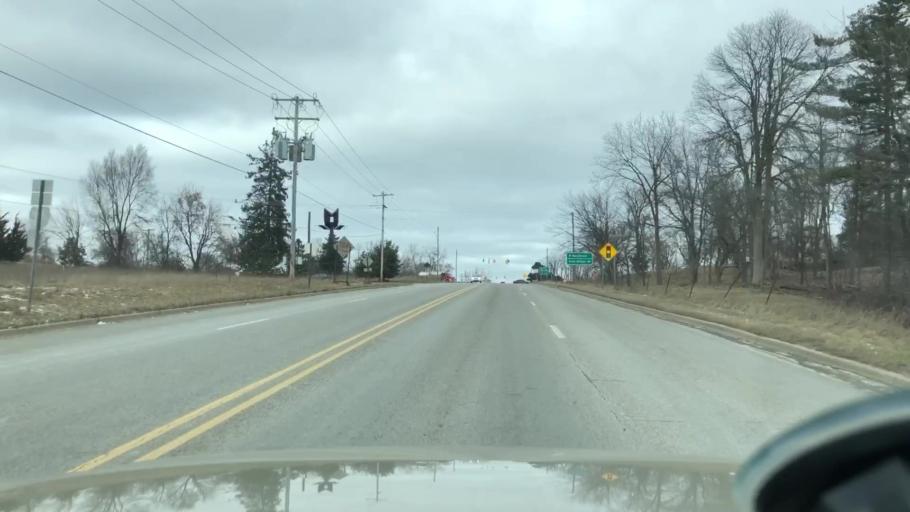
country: US
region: Michigan
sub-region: Jackson County
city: Jackson
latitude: 42.2730
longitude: -84.3844
